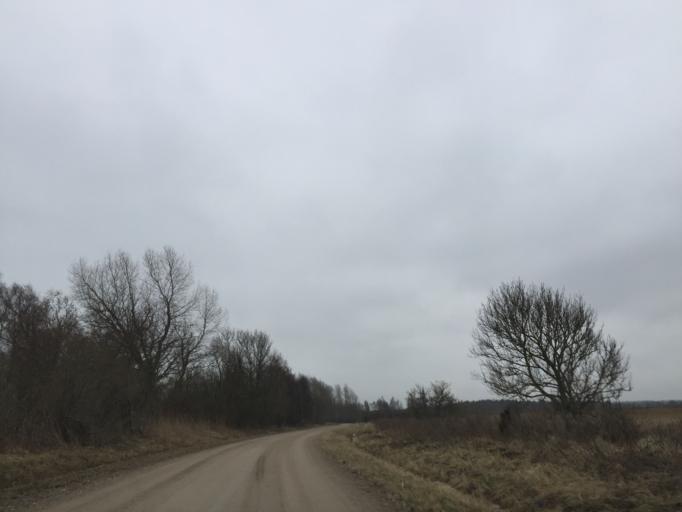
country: EE
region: Saare
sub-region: Kuressaare linn
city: Kuressaare
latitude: 58.1401
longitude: 22.2256
